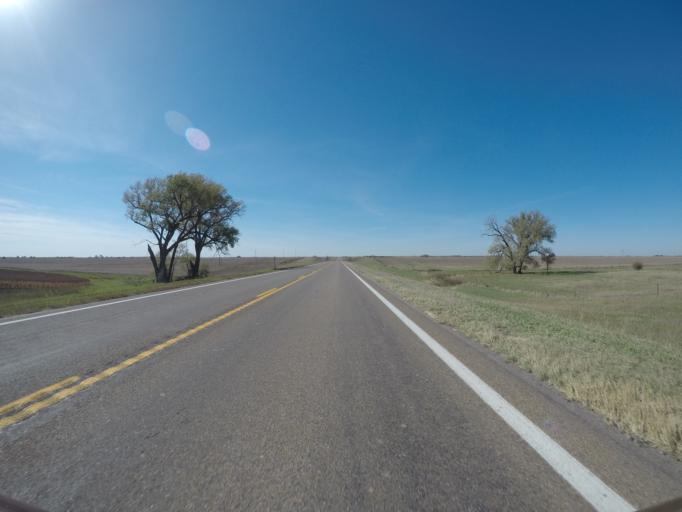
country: US
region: Kansas
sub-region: Smith County
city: Smith Center
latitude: 39.7711
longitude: -98.9607
